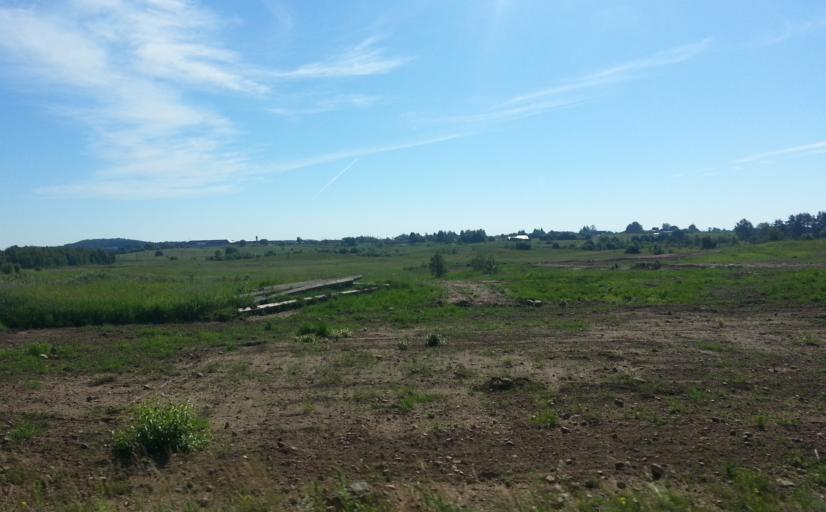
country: LT
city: Grigiskes
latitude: 54.7696
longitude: 25.0799
